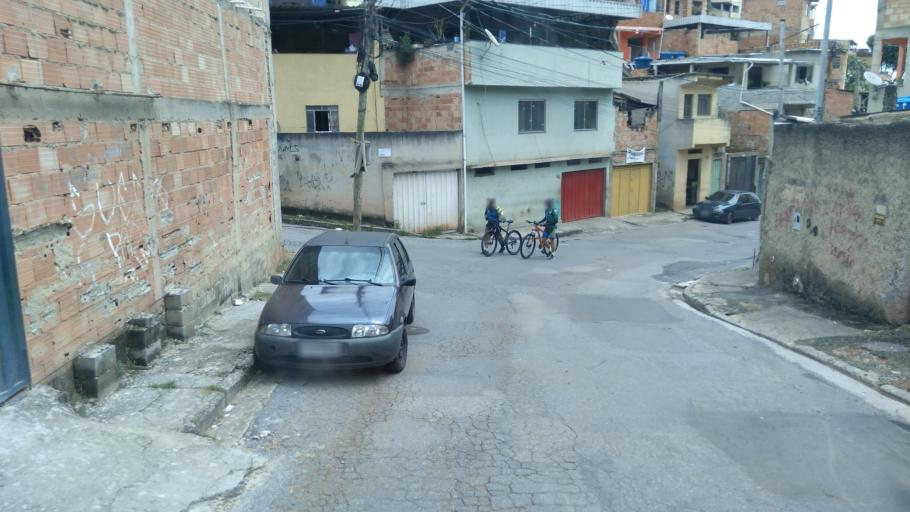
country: BR
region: Minas Gerais
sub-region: Belo Horizonte
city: Belo Horizonte
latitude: -19.8503
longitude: -43.8916
